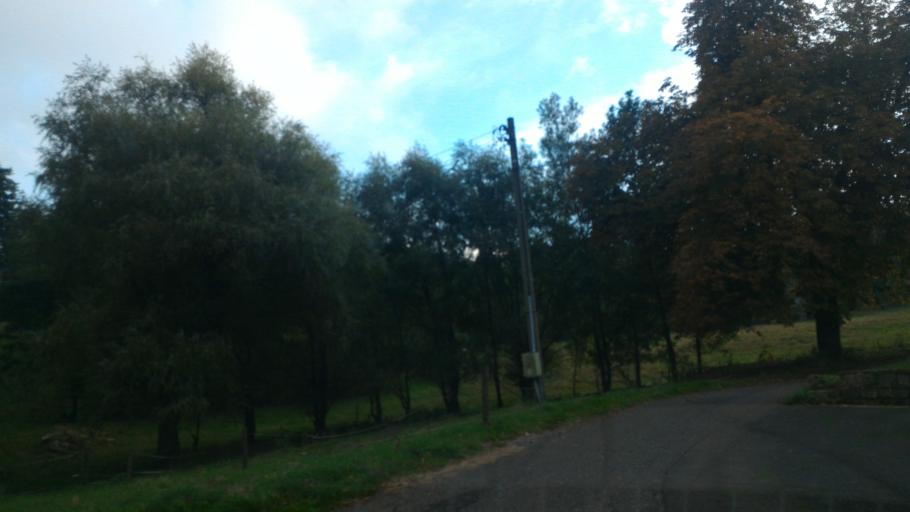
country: CZ
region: Ustecky
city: Dolni Podluzi
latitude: 50.8628
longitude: 14.5732
